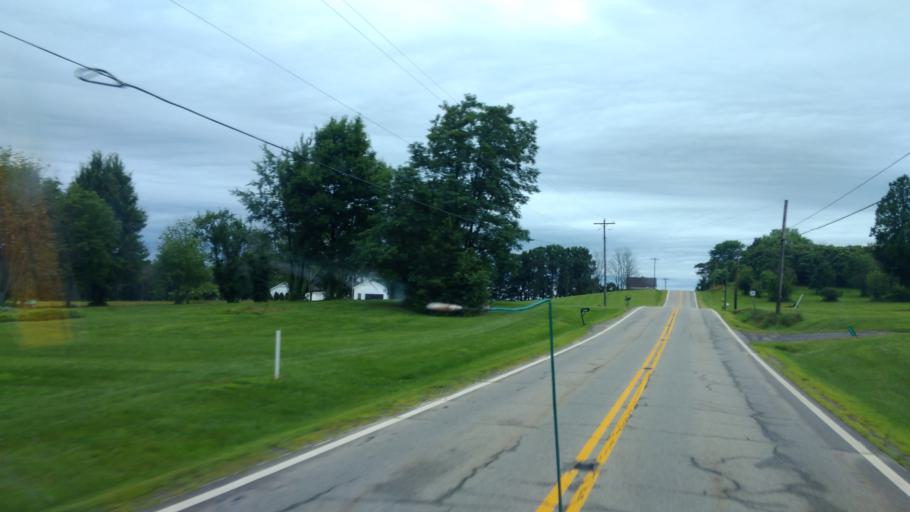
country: US
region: Ohio
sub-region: Carroll County
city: Carrollton
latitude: 40.6370
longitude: -81.0652
